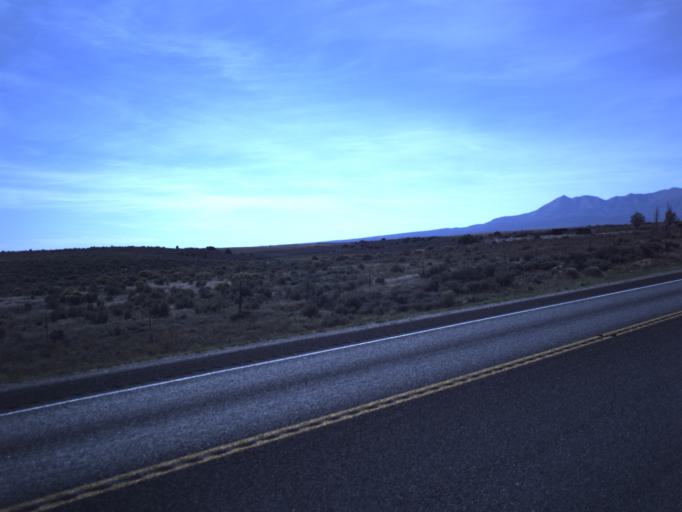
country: US
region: Utah
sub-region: San Juan County
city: Monticello
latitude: 37.8445
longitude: -109.1400
